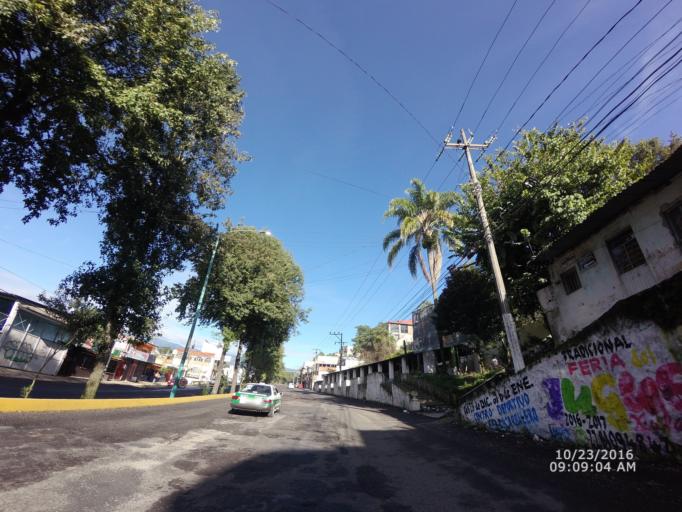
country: TR
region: Canakkale
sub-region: Goekceada
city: Gokceada
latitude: 40.2203
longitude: 26.0301
